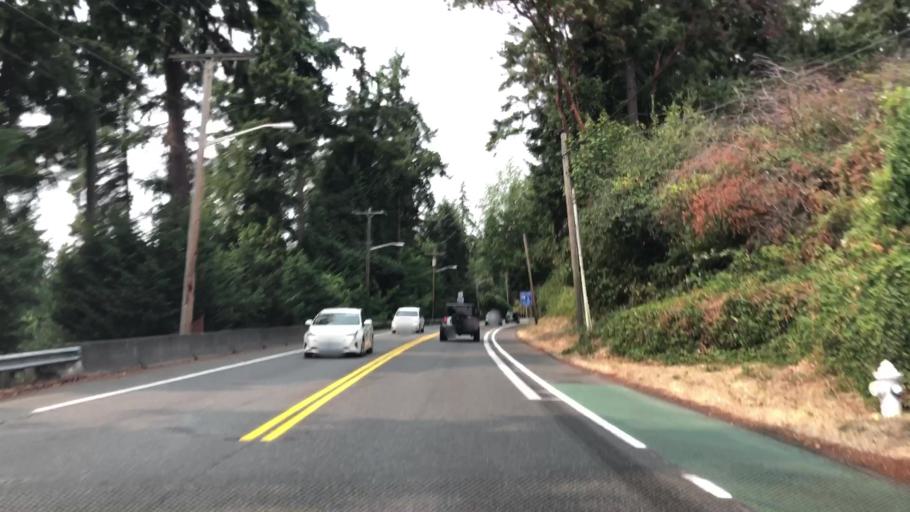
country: US
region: Washington
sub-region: King County
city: Inglewood-Finn Hill
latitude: 47.7011
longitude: -122.2353
